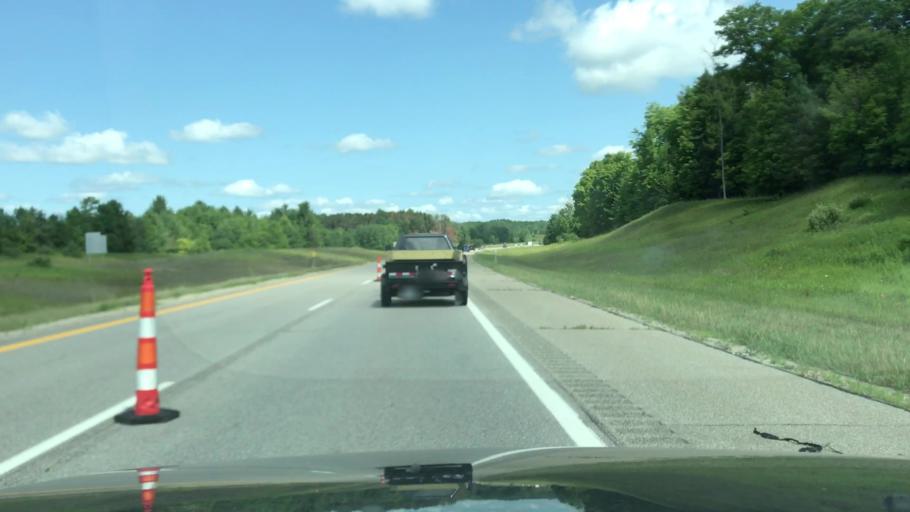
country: US
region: Michigan
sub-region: Mecosta County
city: Big Rapids
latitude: 43.7621
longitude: -85.5327
